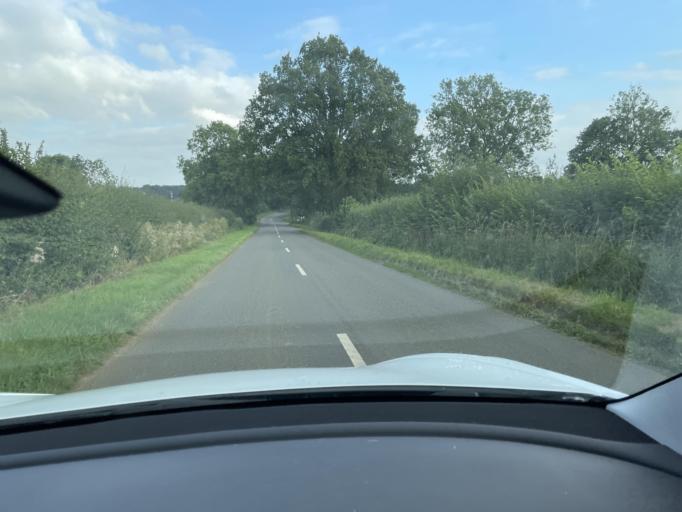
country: GB
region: England
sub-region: Leicestershire
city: Market Harborough
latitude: 52.4032
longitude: -1.0029
